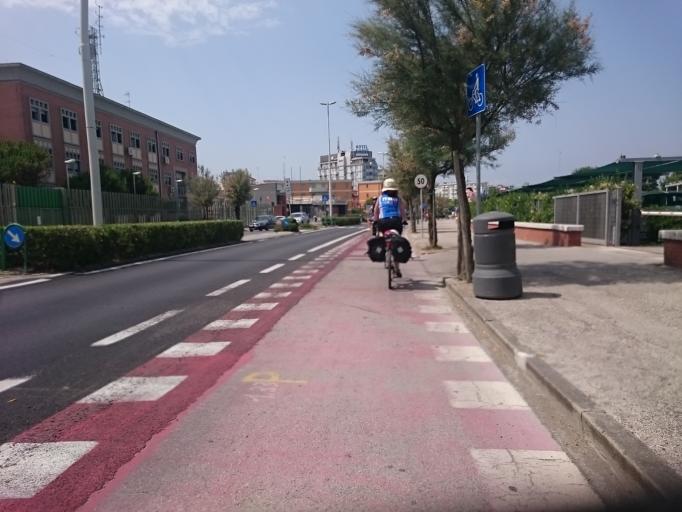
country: IT
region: Veneto
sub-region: Provincia di Venezia
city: Chioggia
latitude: 45.2092
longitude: 12.2966
